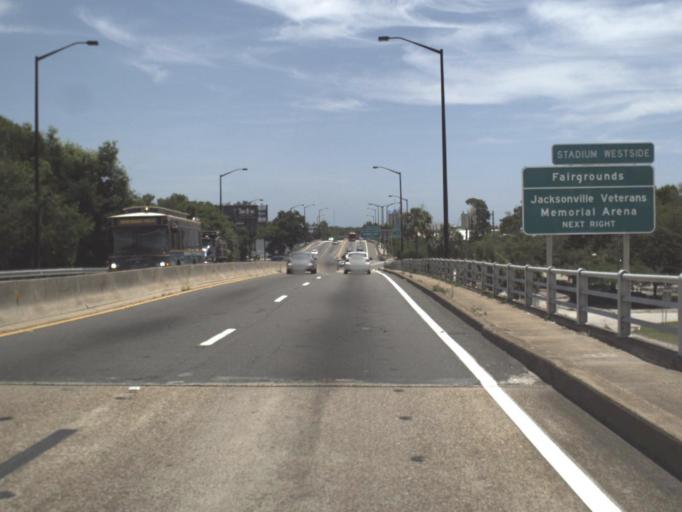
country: US
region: Florida
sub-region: Duval County
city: Jacksonville
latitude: 30.3292
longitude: -81.6468
